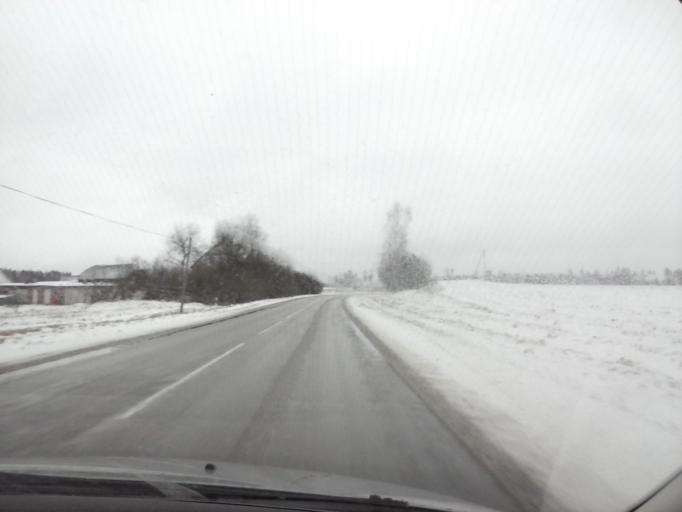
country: LV
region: Valkas Rajons
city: Valka
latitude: 57.7397
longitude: 25.9456
